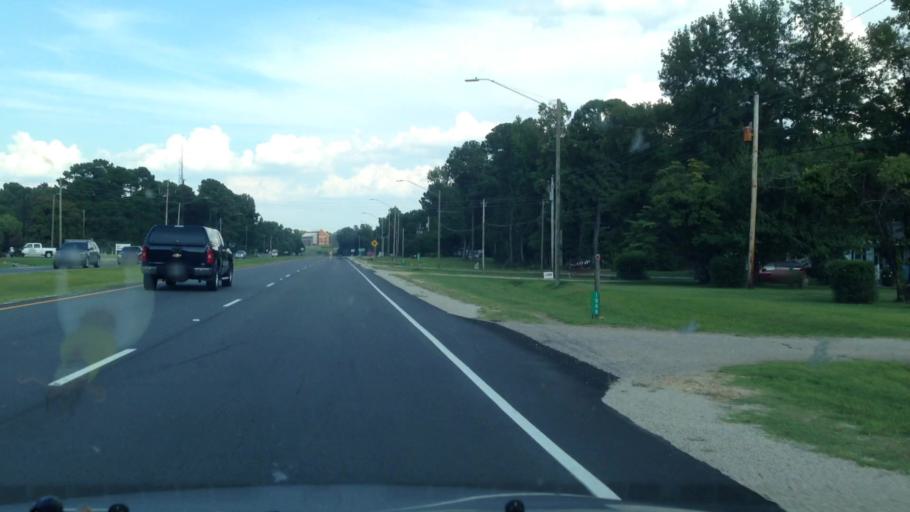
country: US
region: North Carolina
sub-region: Harnett County
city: Buies Creek
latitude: 35.4086
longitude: -78.7721
